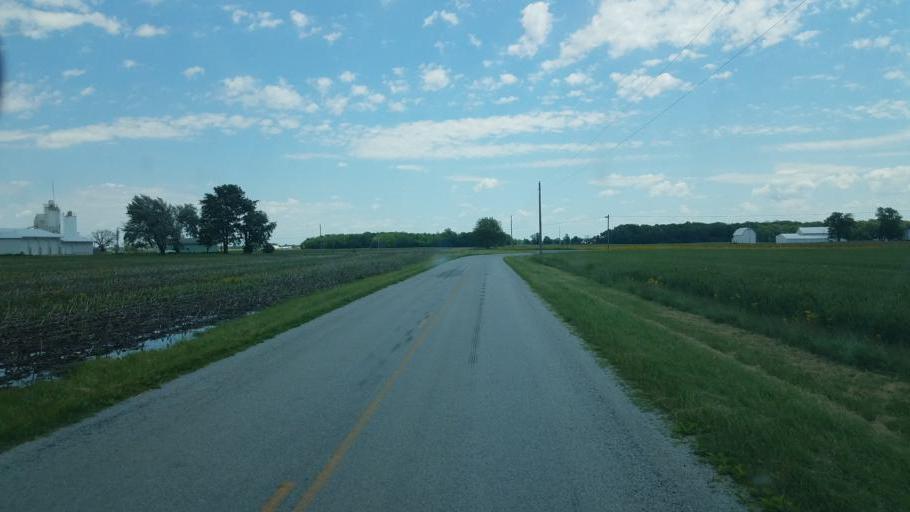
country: US
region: Ohio
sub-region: Hardin County
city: Forest
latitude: 40.6730
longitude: -83.4442
